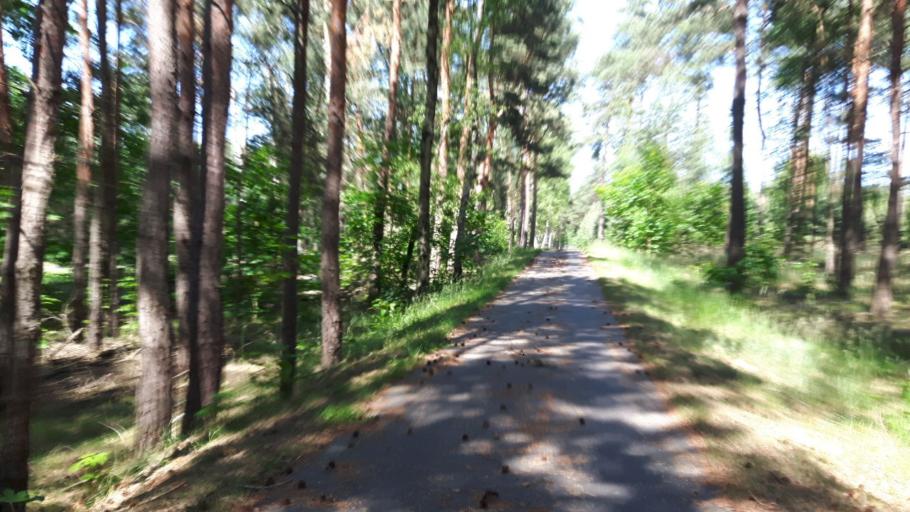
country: DE
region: Brandenburg
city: Treuenbrietzen
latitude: 52.0640
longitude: 12.8280
